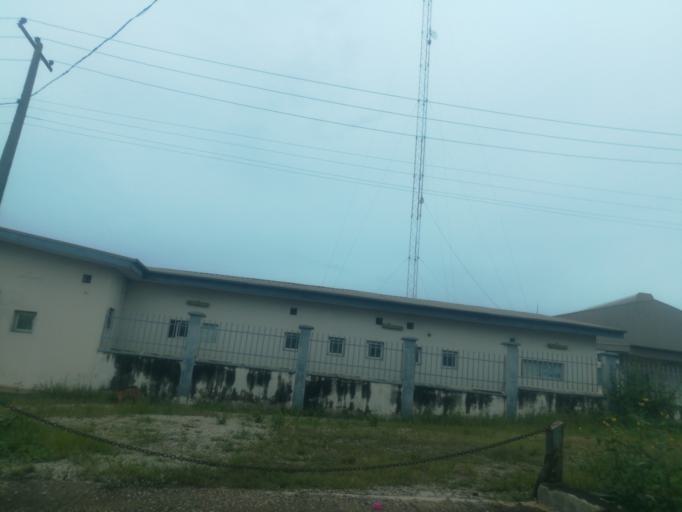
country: NG
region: Oyo
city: Ibadan
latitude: 7.3327
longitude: 3.8843
